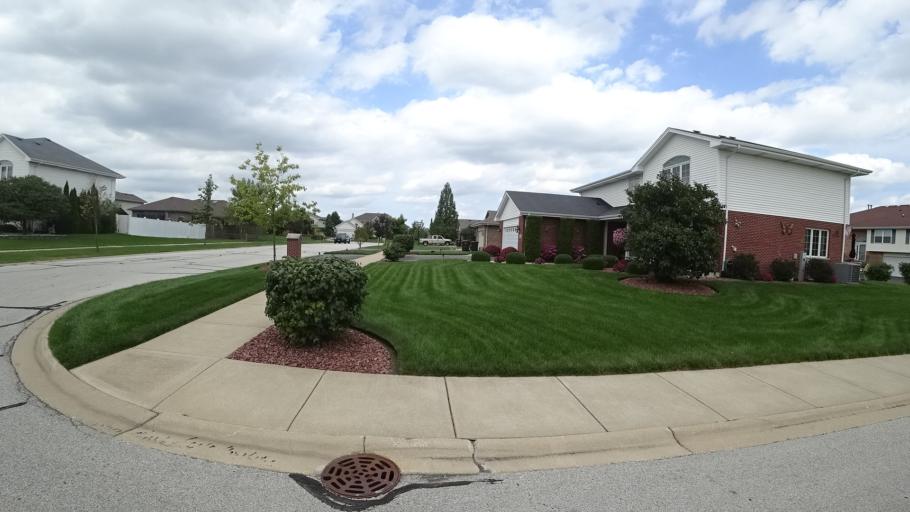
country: US
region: Illinois
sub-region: Cook County
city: Orland Hills
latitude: 41.5588
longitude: -87.8268
